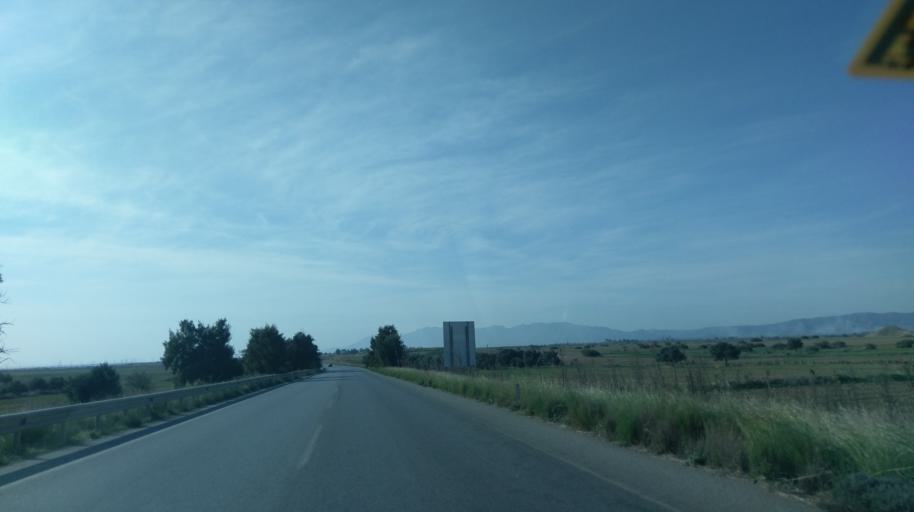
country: CY
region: Ammochostos
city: Lefkonoiko
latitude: 35.2613
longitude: 33.7773
